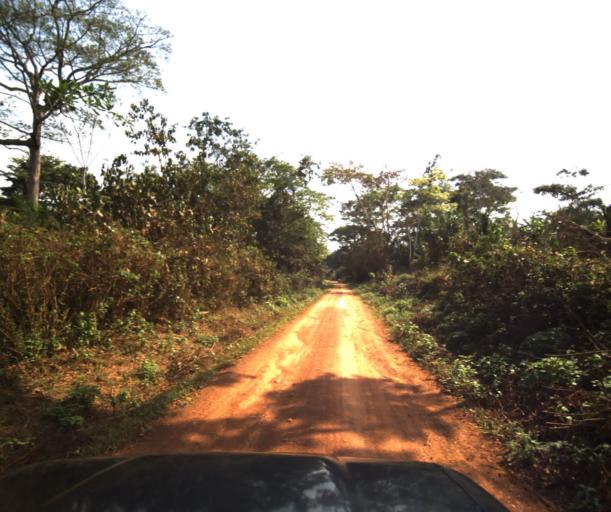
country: CM
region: Centre
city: Akono
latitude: 3.6011
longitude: 11.2386
